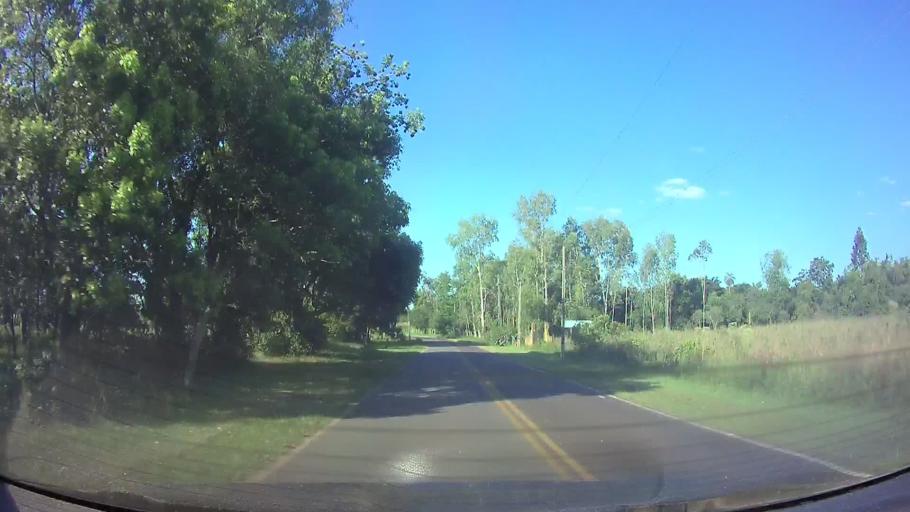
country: PY
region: Cordillera
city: Atyra
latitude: -25.3026
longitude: -57.1860
